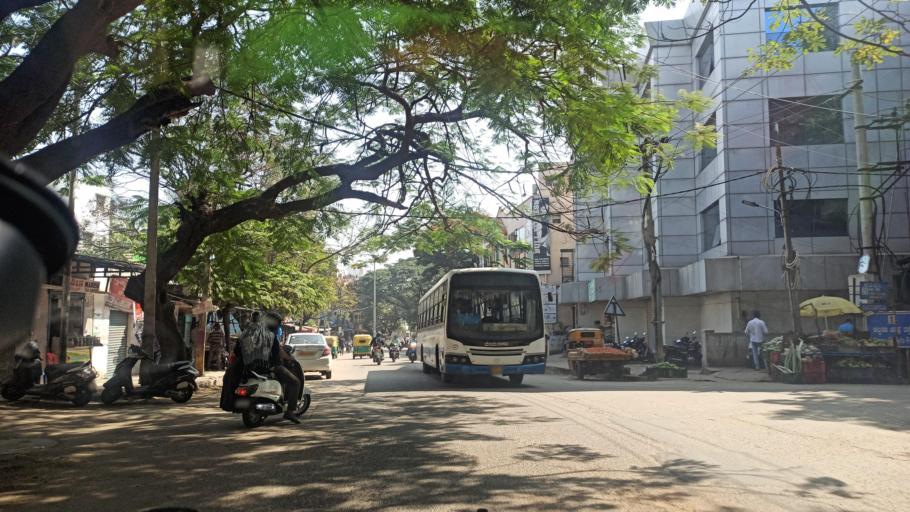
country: IN
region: Karnataka
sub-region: Bangalore Urban
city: Yelahanka
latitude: 13.0425
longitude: 77.5798
